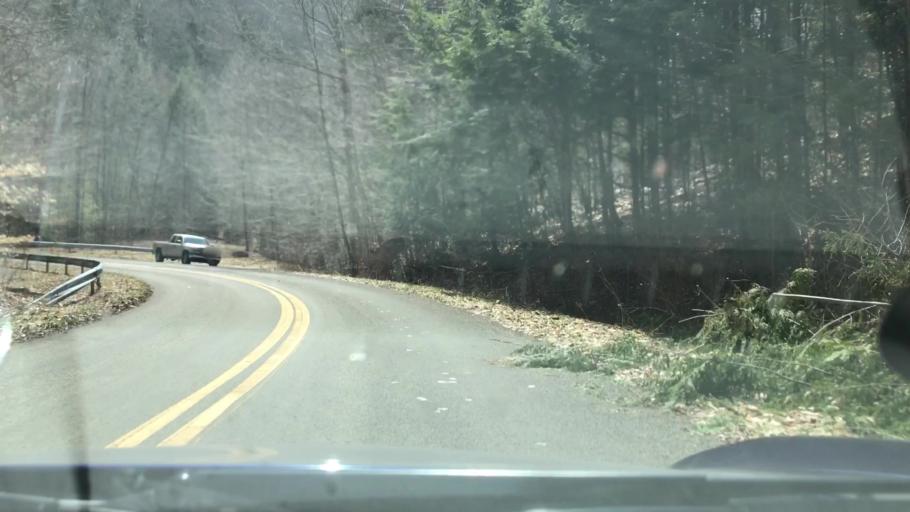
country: US
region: Pennsylvania
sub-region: Warren County
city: Sheffield
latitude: 41.8097
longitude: -78.9364
